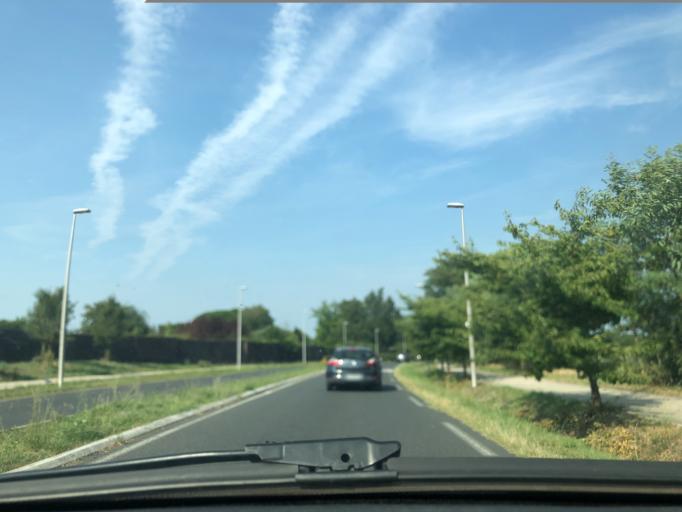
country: FR
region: Aquitaine
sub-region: Departement de la Gironde
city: Pessac
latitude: 44.8224
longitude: -0.6459
